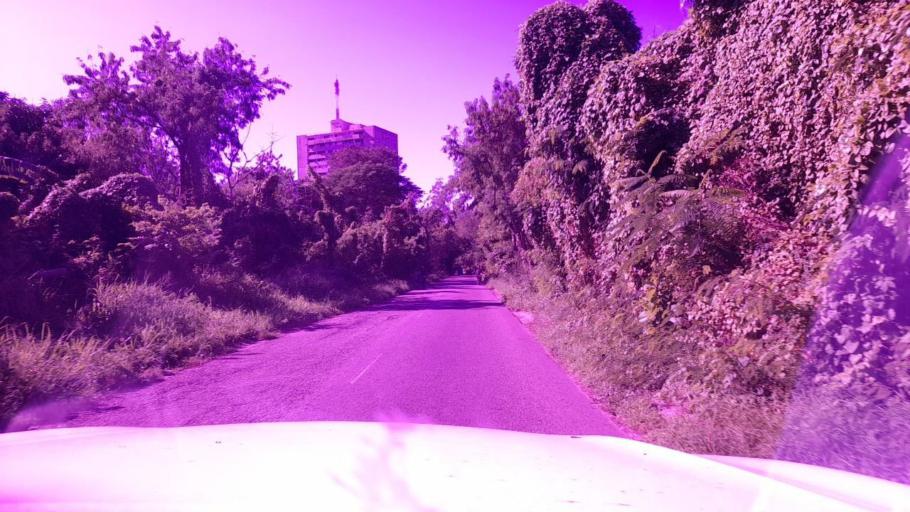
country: CU
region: La Habana
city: Alamar
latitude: 23.1643
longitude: -82.2749
